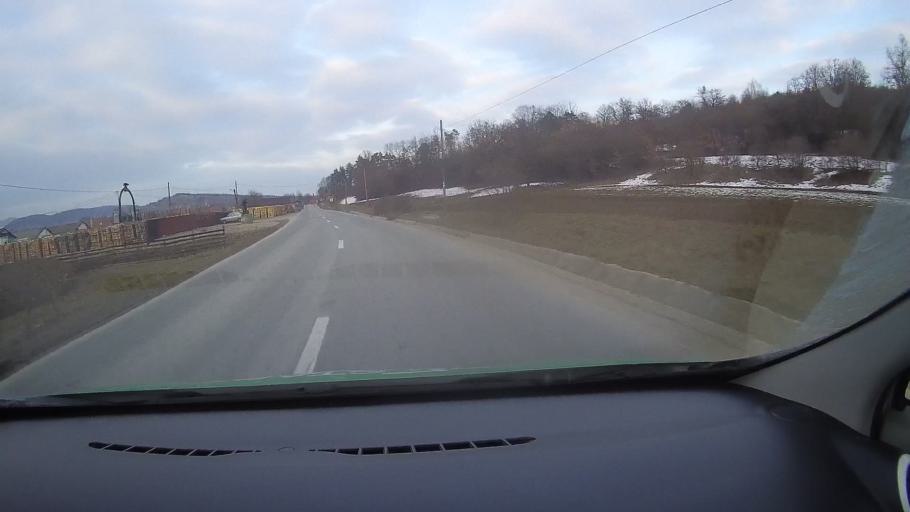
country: RO
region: Harghita
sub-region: Comuna Simonesti
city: Simonesti
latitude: 46.3507
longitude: 25.1291
